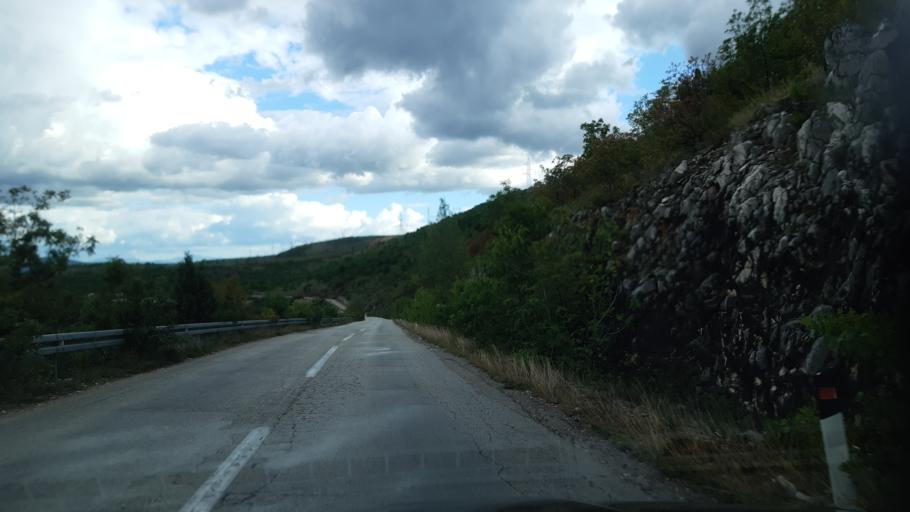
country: BA
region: Federation of Bosnia and Herzegovina
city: Rodoc
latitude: 43.3081
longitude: 17.7802
